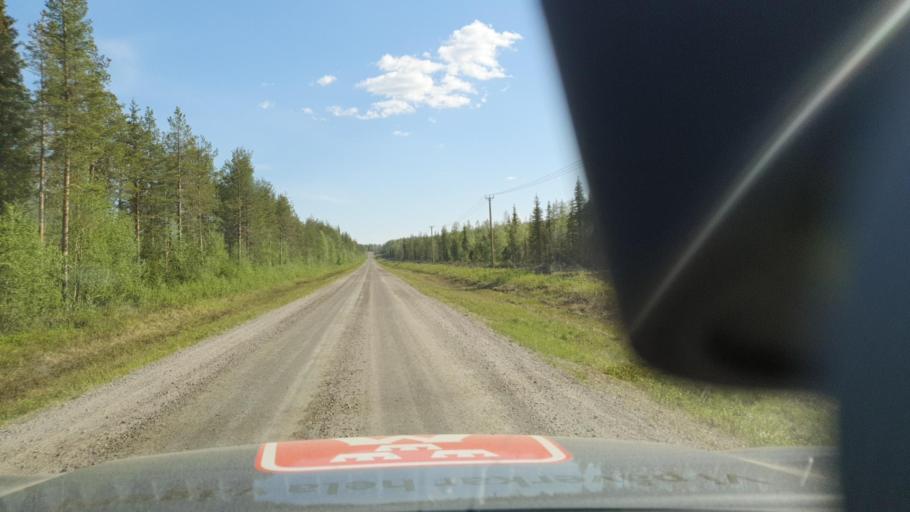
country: SE
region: Norrbotten
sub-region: Bodens Kommun
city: Boden
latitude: 66.5032
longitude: 21.9079
